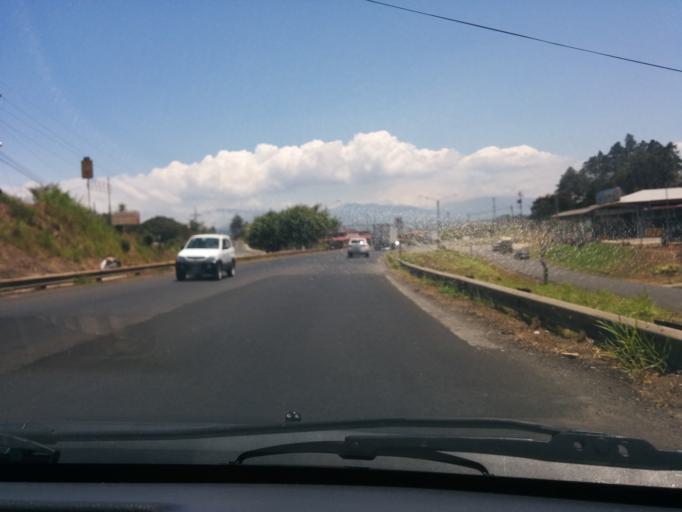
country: CR
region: Alajuela
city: San Rafael
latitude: 10.0749
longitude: -84.4810
